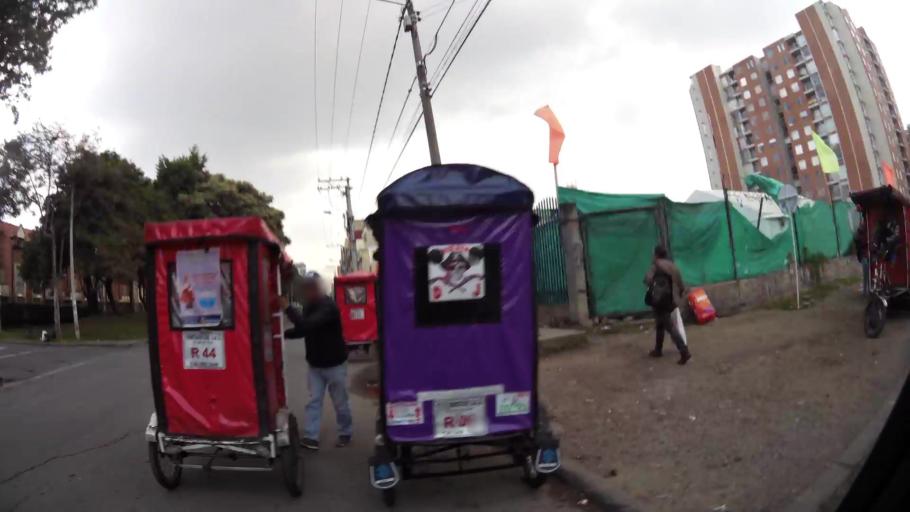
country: CO
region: Cundinamarca
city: Cota
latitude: 4.7450
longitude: -74.0569
